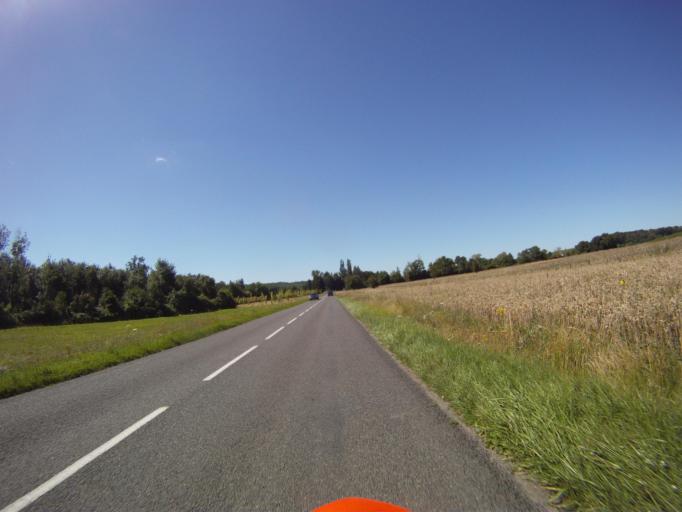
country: FR
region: Centre
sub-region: Departement d'Indre-et-Loire
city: Vernou-sur-Brenne
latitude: 47.4119
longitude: 0.8275
